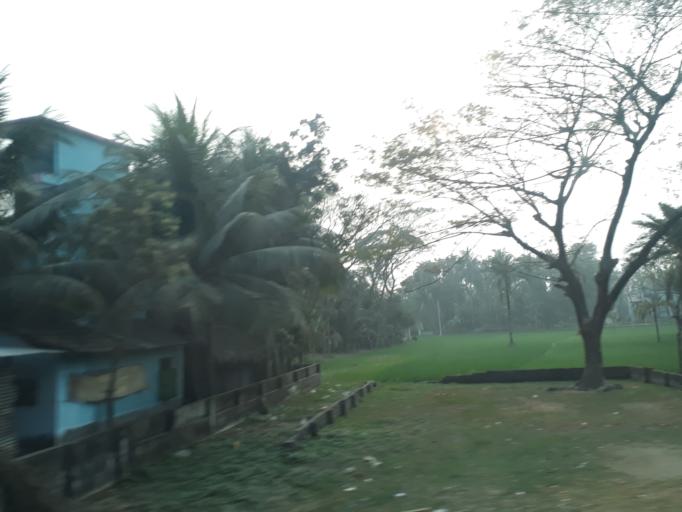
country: BD
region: Khulna
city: Bhatpara Abhaynagar
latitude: 22.9309
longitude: 89.4925
